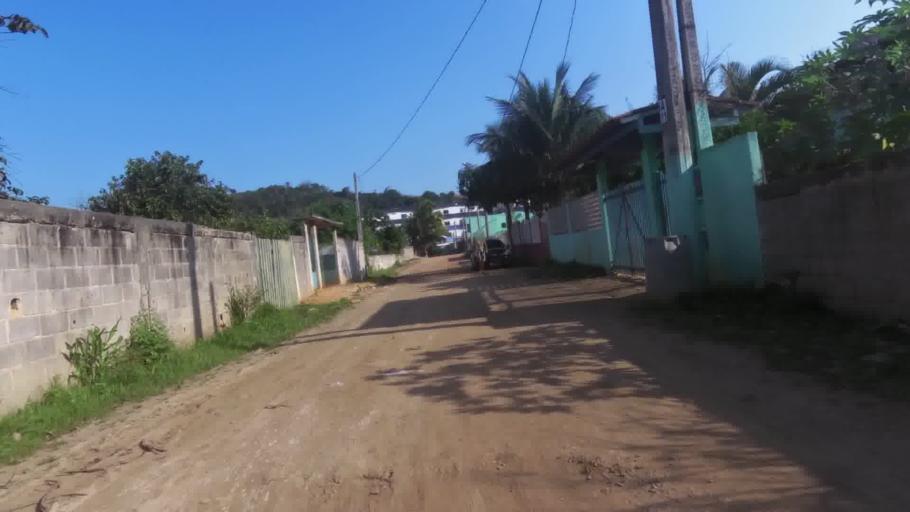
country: BR
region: Espirito Santo
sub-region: Piuma
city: Piuma
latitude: -20.8647
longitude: -40.7595
